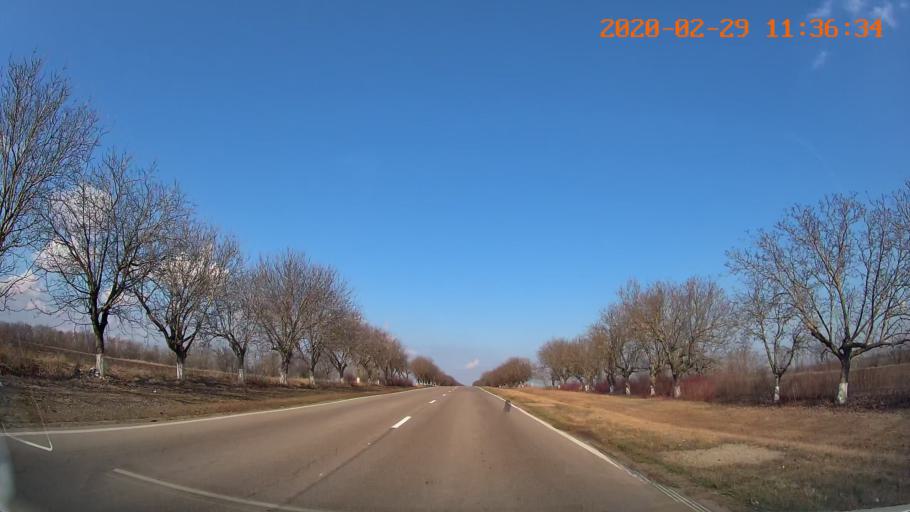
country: MD
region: Rezina
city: Saharna
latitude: 47.5979
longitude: 29.0545
